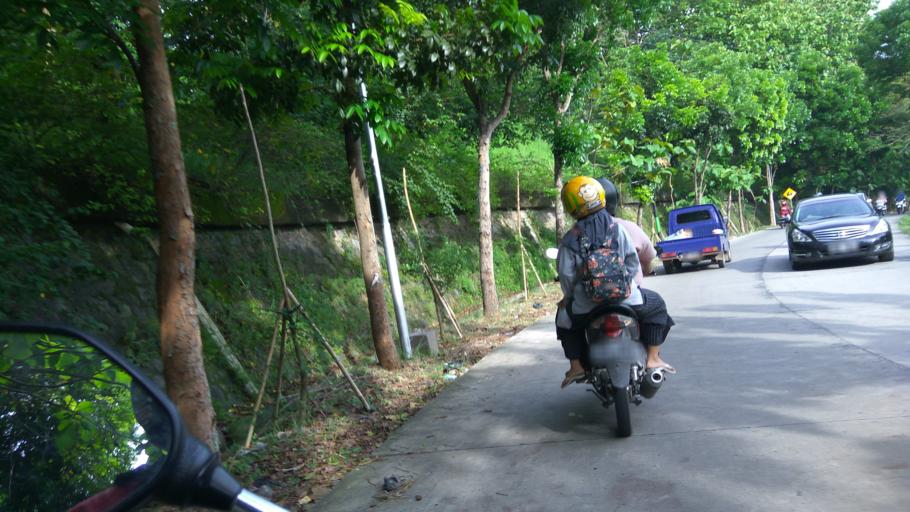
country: ID
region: Central Java
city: Mranggen
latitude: -7.0487
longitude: 110.4645
